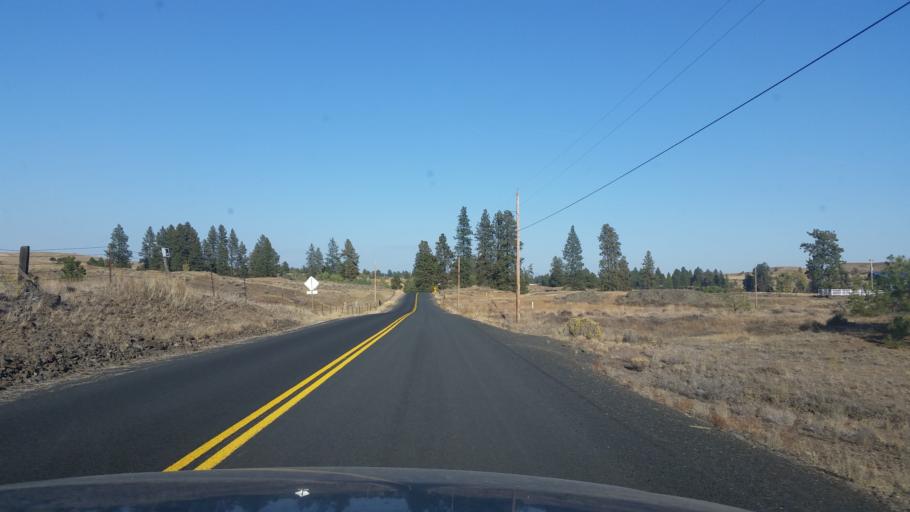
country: US
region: Washington
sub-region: Spokane County
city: Cheney
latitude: 47.3428
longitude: -117.7307
